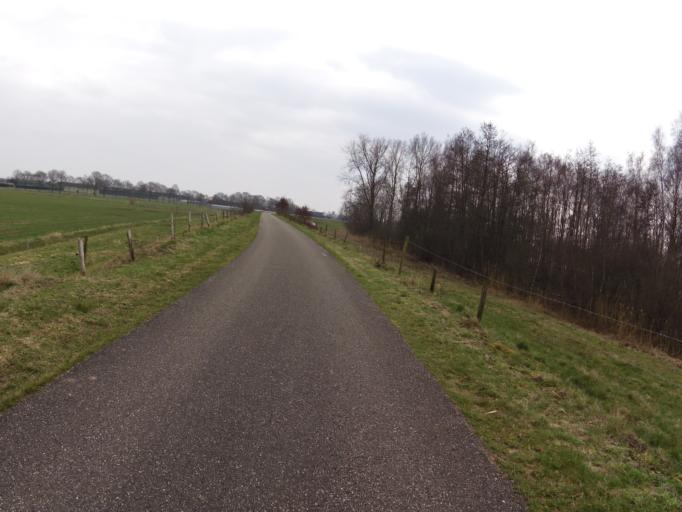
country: NL
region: North Brabant
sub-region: Gemeente Heusden
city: Heusden
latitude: 51.7027
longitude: 5.1147
